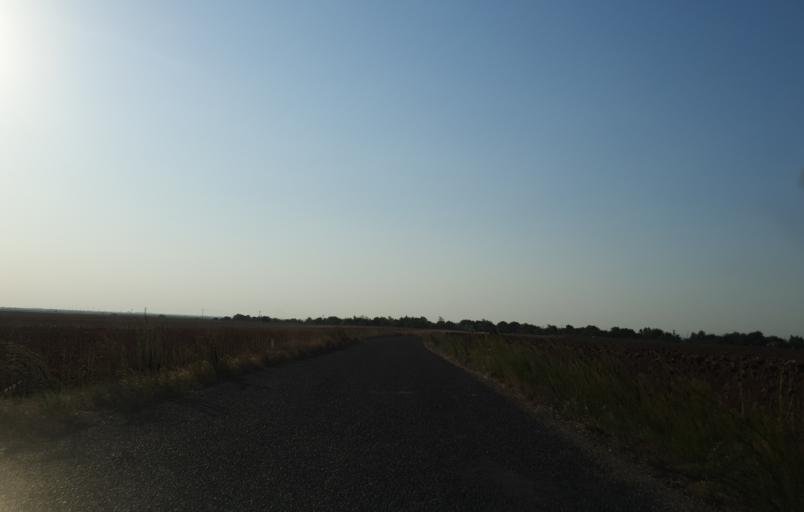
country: TR
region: Tekirdag
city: Beyazkoy
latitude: 41.4284
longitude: 27.7596
